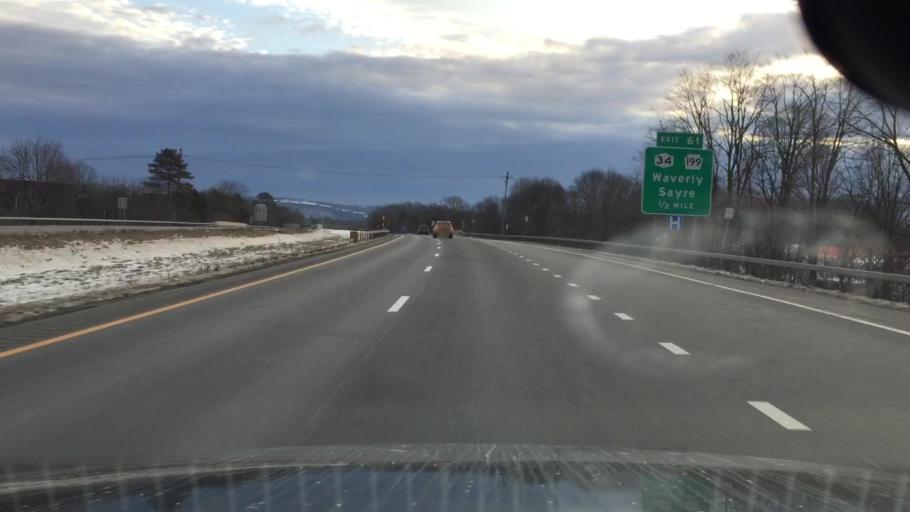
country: US
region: Pennsylvania
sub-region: Bradford County
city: South Waverly
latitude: 41.9986
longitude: -76.5432
